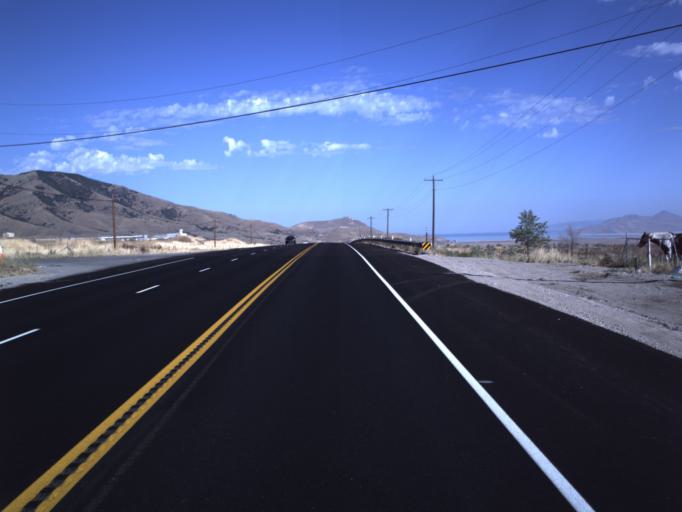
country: US
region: Utah
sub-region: Salt Lake County
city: Oquirrh
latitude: 40.6459
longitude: -112.0671
